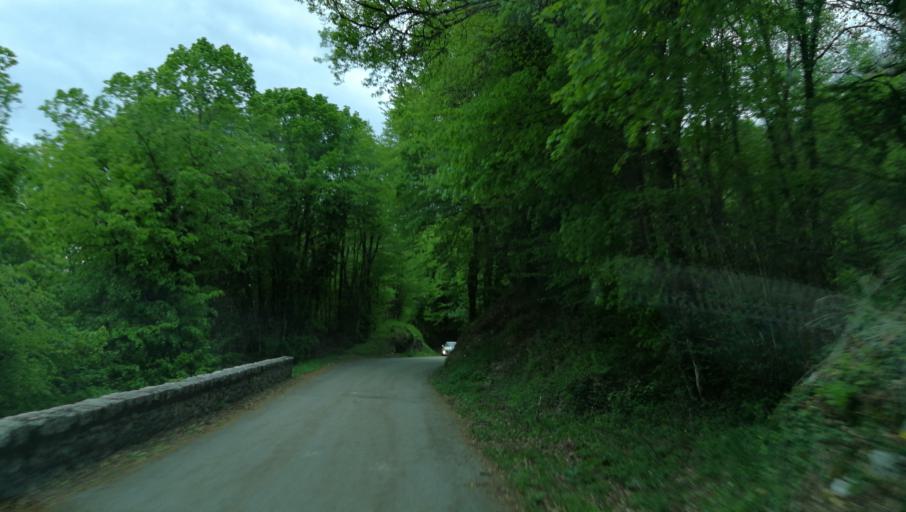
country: FR
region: Rhone-Alpes
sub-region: Departement de la Savoie
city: Chatillon
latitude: 45.7537
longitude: 5.8298
